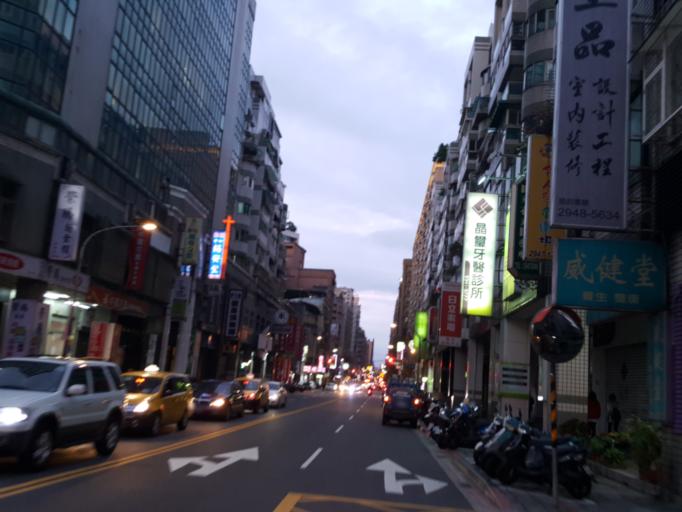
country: TW
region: Taipei
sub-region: Taipei
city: Banqiao
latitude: 24.9967
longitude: 121.5070
